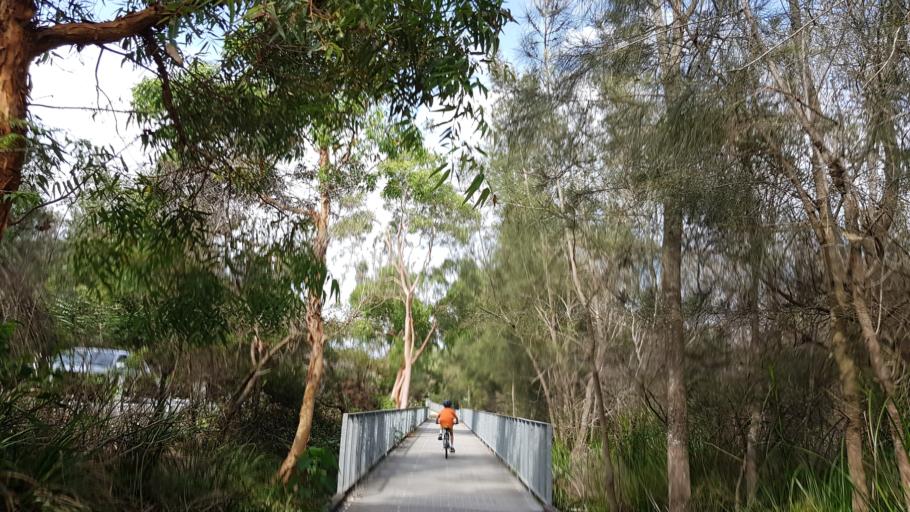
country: AU
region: New South Wales
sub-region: Pittwater
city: North Narrabeen
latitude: -33.7116
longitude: 151.2743
